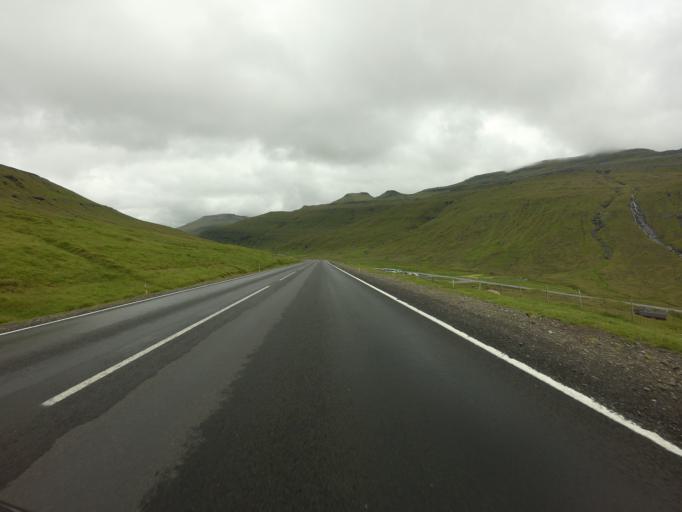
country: FO
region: Streymoy
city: Kollafjordhur
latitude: 62.1158
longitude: -6.9836
